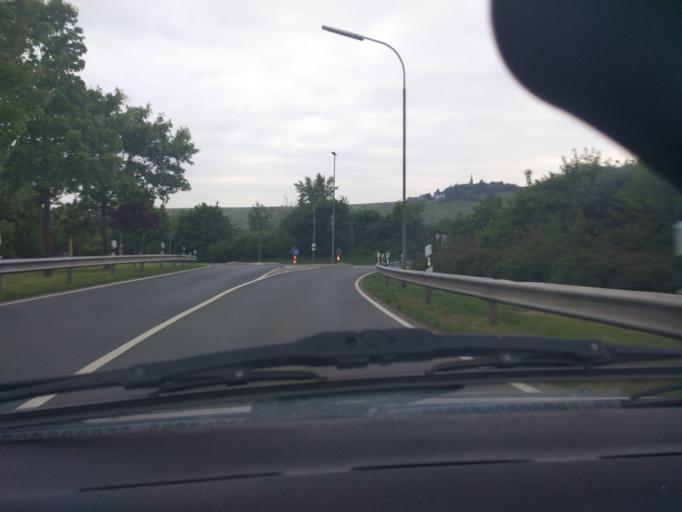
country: DE
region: Hesse
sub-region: Regierungsbezirk Darmstadt
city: Rudesheim am Rhein
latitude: 49.9676
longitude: 7.9439
